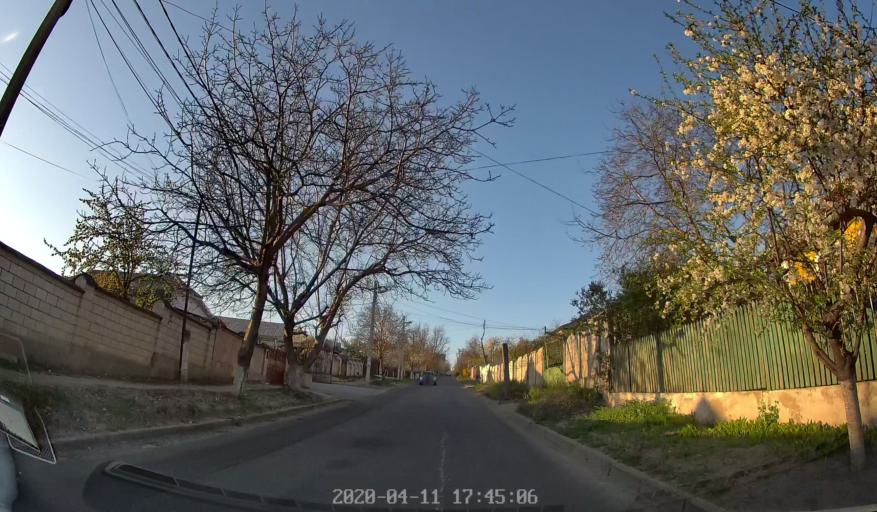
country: MD
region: Chisinau
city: Chisinau
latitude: 46.9824
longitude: 28.8230
